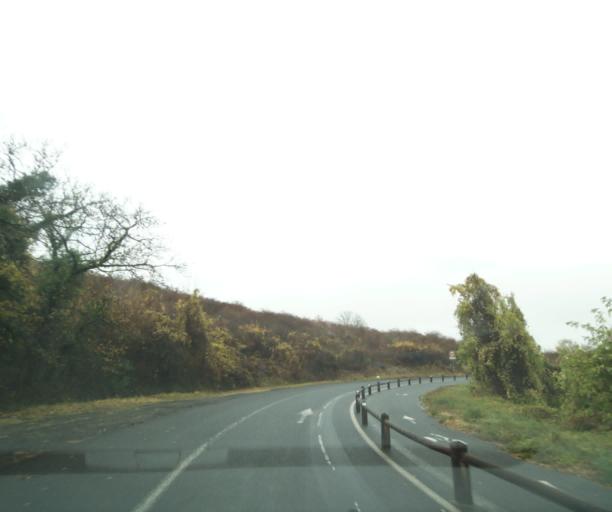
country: FR
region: Auvergne
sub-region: Departement du Puy-de-Dome
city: Cournon-d'Auvergne
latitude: 45.7573
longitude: 3.2063
